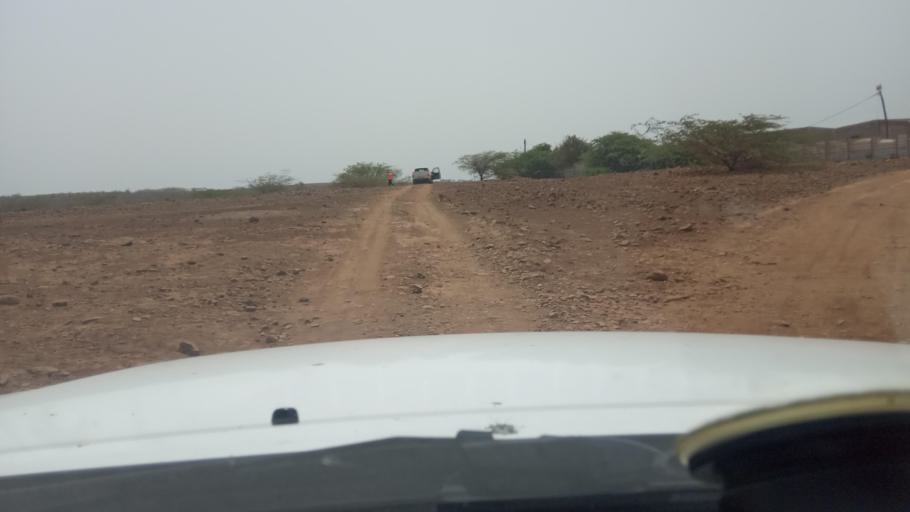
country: CV
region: Ribeira Grande de Santiago
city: Cidade Velha
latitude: 14.9501
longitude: -23.6021
